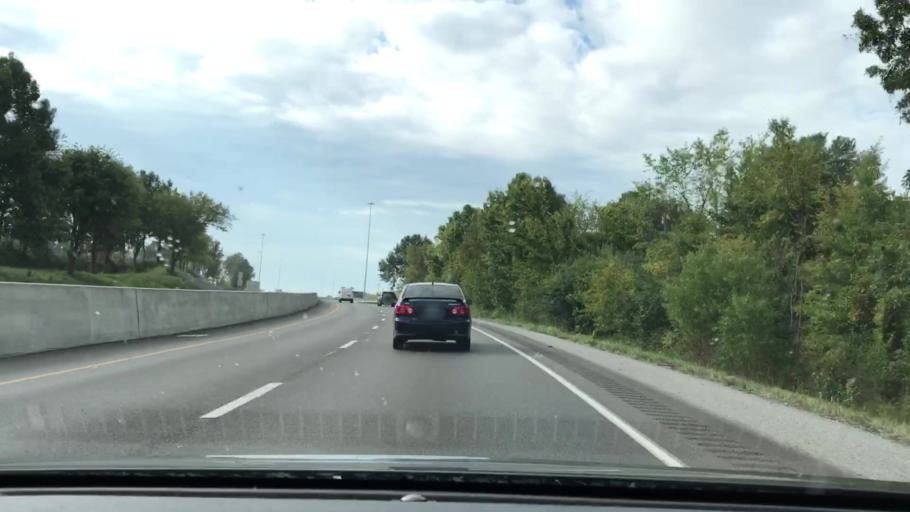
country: US
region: Kentucky
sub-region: Graves County
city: Mayfield
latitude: 36.7471
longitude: -88.6677
